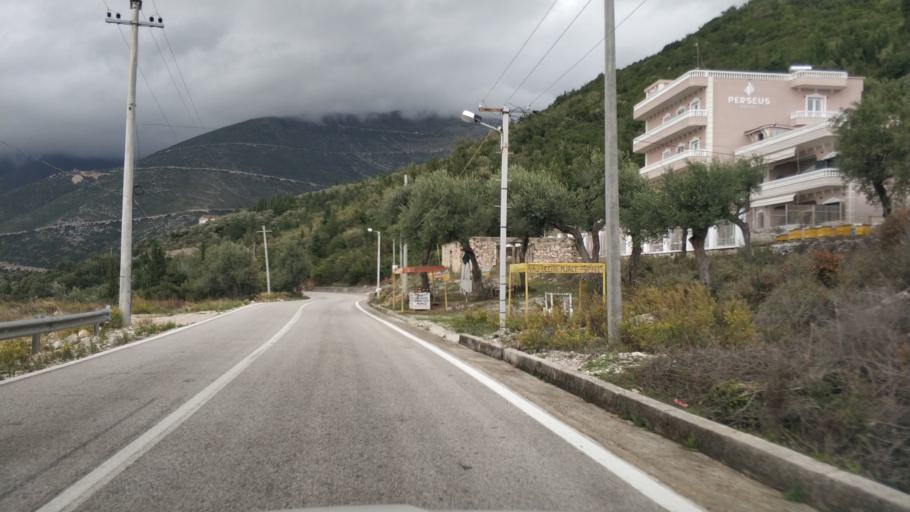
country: AL
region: Vlore
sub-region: Rrethi i Vlores
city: Vranisht
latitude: 40.1671
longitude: 19.6195
